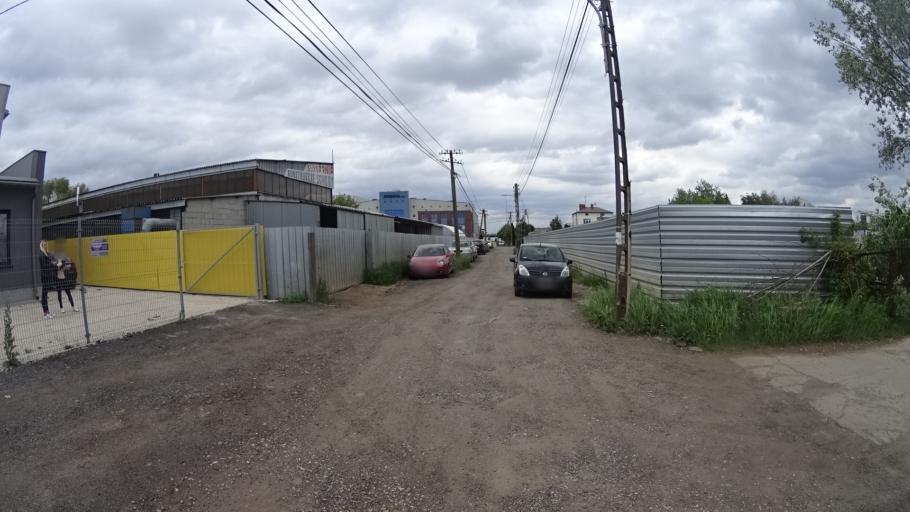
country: PL
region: Masovian Voivodeship
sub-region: Warszawa
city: Ursus
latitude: 52.2171
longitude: 20.8583
